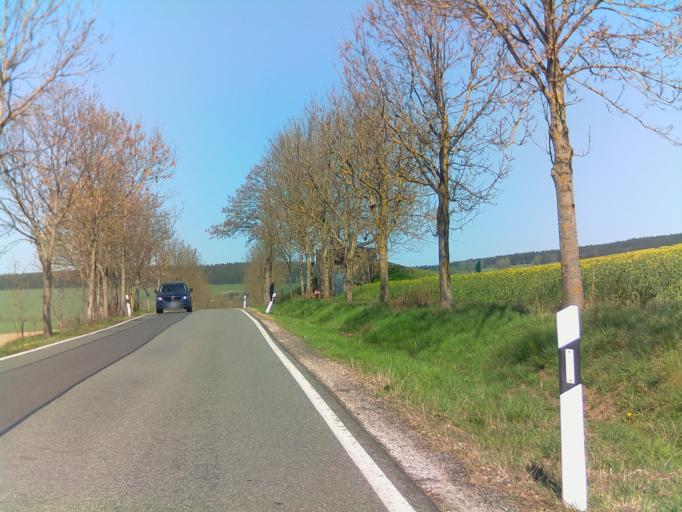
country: DE
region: Thuringia
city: Friedersdorf
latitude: 50.5951
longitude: 11.0364
